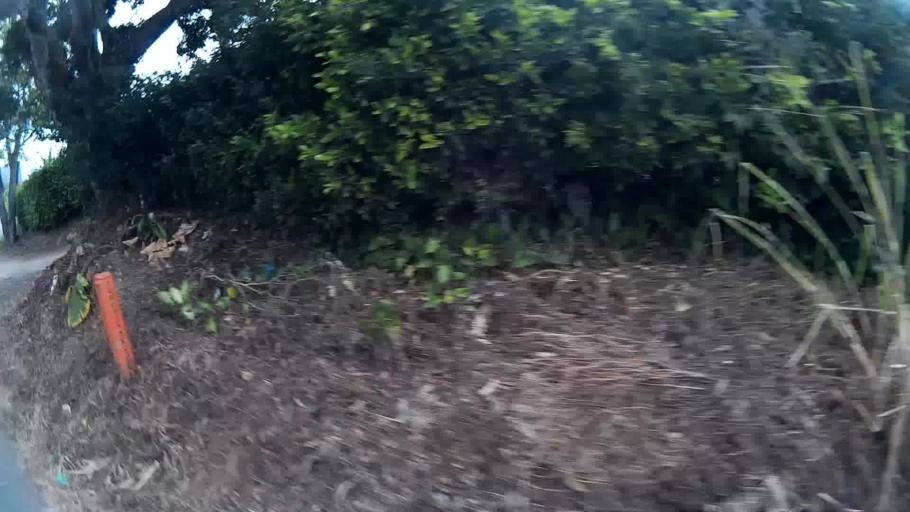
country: CO
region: Risaralda
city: Pereira
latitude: 4.8385
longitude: -75.7566
